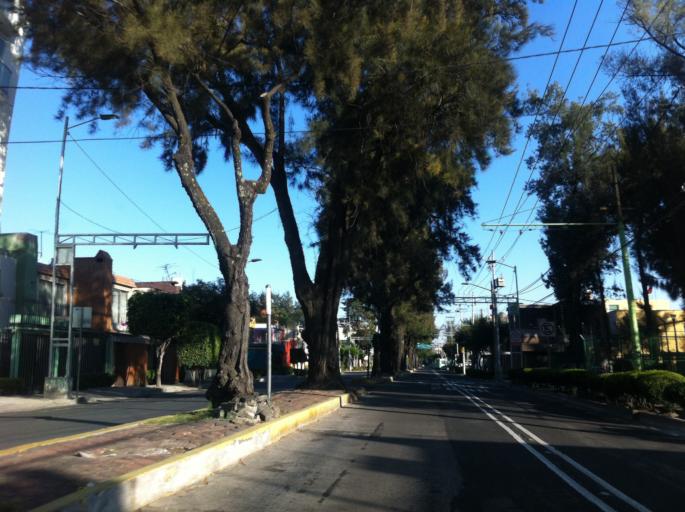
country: MX
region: Mexico City
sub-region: Iztacalco
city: Iztacalco
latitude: 19.4123
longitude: -99.1034
